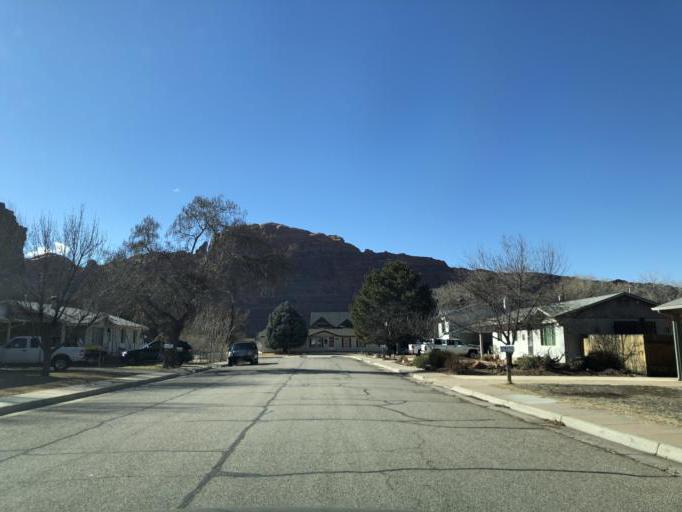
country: US
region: Utah
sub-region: Grand County
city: Moab
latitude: 38.5755
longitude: -109.5648
